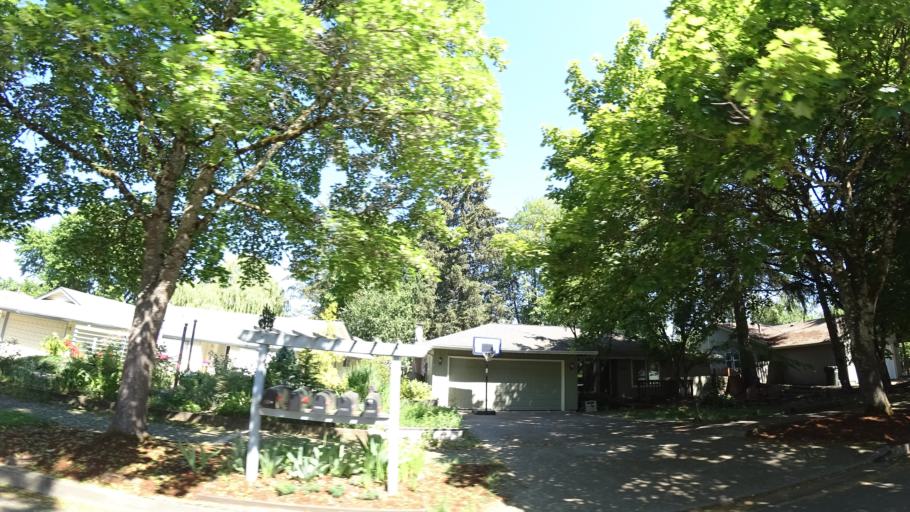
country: US
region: Oregon
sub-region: Washington County
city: Tigard
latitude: 45.4511
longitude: -122.8006
